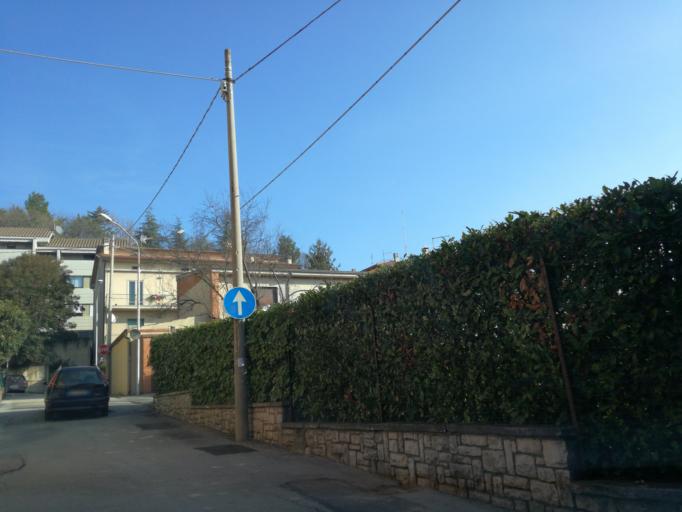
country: IT
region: Umbria
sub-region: Provincia di Perugia
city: Perugia
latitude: 43.1085
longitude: 12.3737
